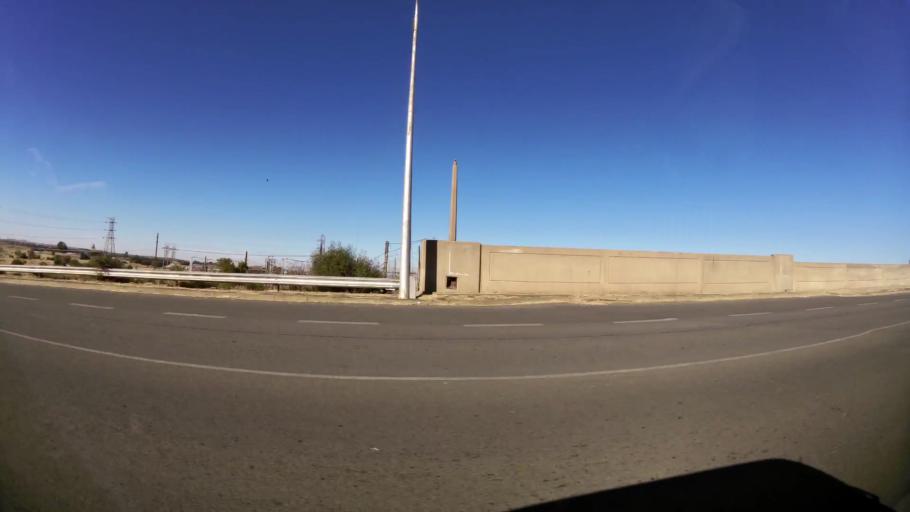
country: ZA
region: Northern Cape
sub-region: Frances Baard District Municipality
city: Kimberley
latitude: -28.7481
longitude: 24.7909
